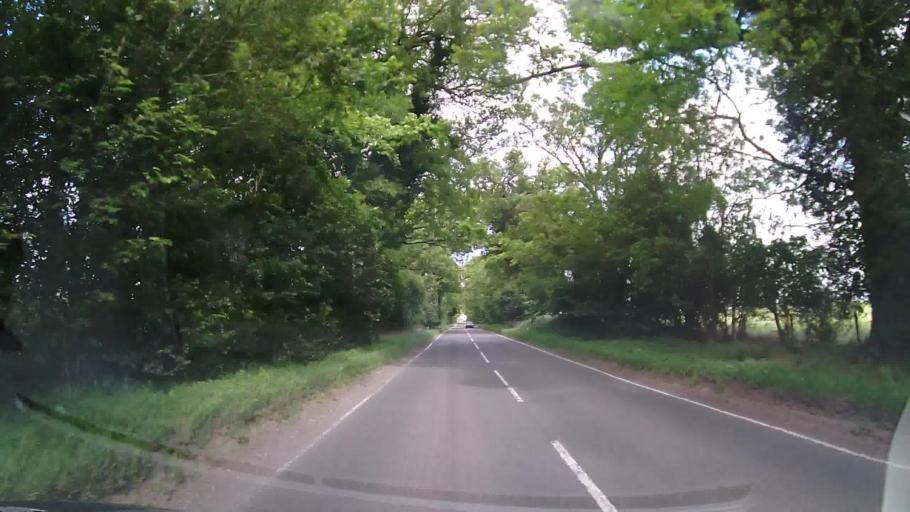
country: GB
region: England
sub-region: Shropshire
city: Whittington
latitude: 52.7925
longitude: -2.9737
